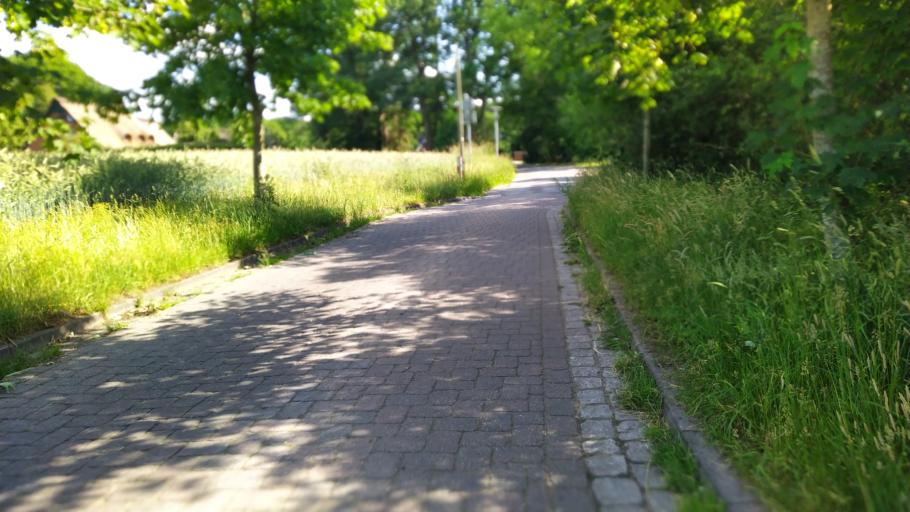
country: DE
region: Lower Saxony
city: Lintig
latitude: 53.6296
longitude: 8.8959
